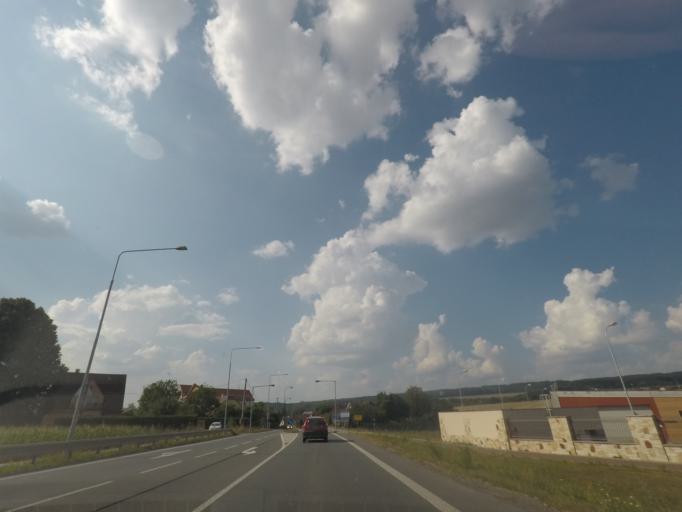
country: CZ
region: Kralovehradecky
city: Dvur Kralove nad Labem
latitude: 50.4206
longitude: 15.8816
